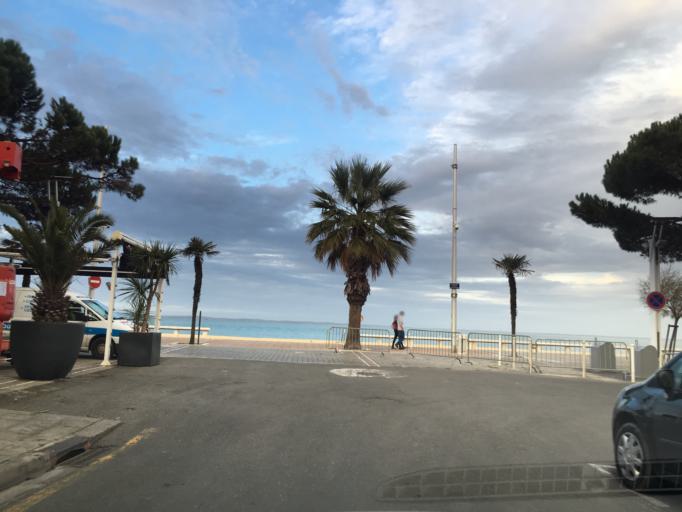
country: FR
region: Aquitaine
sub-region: Departement de la Gironde
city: Arcachon
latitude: 44.6631
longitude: -1.1670
